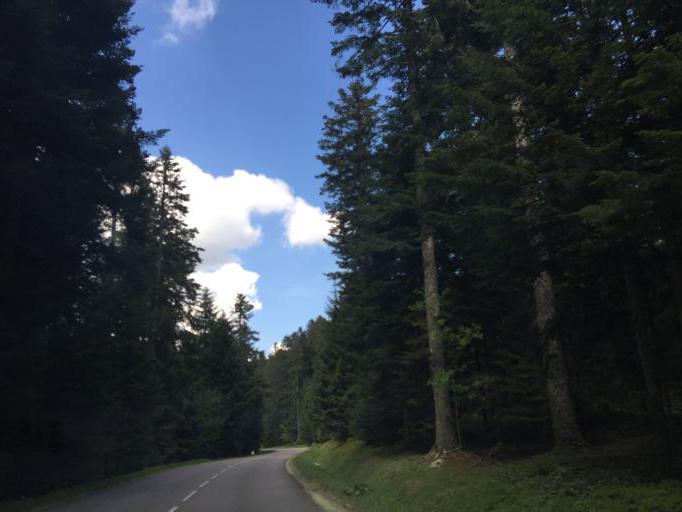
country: FR
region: Rhone-Alpes
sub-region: Departement de la Loire
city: Saint-Genest-Malifaux
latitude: 45.3173
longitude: 4.4672
